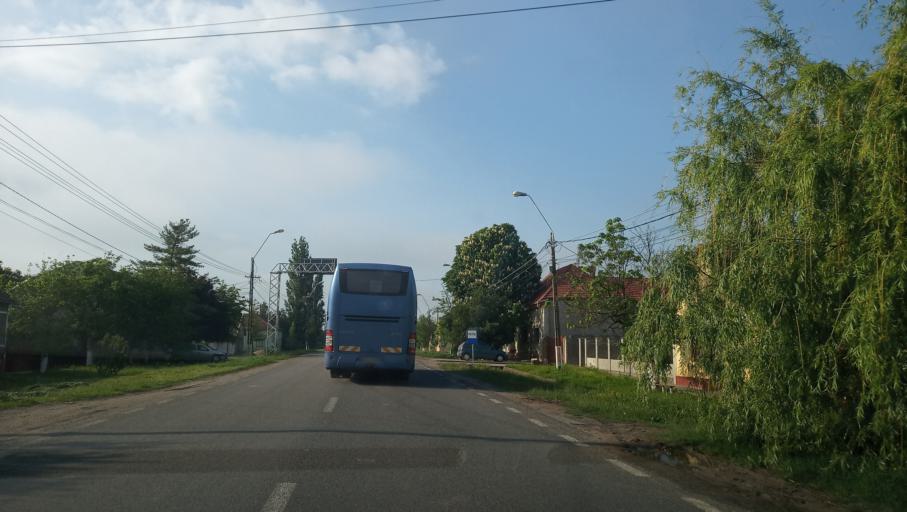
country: RO
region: Timis
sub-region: Comuna Moravita
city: Moravita
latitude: 45.2559
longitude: 21.2670
